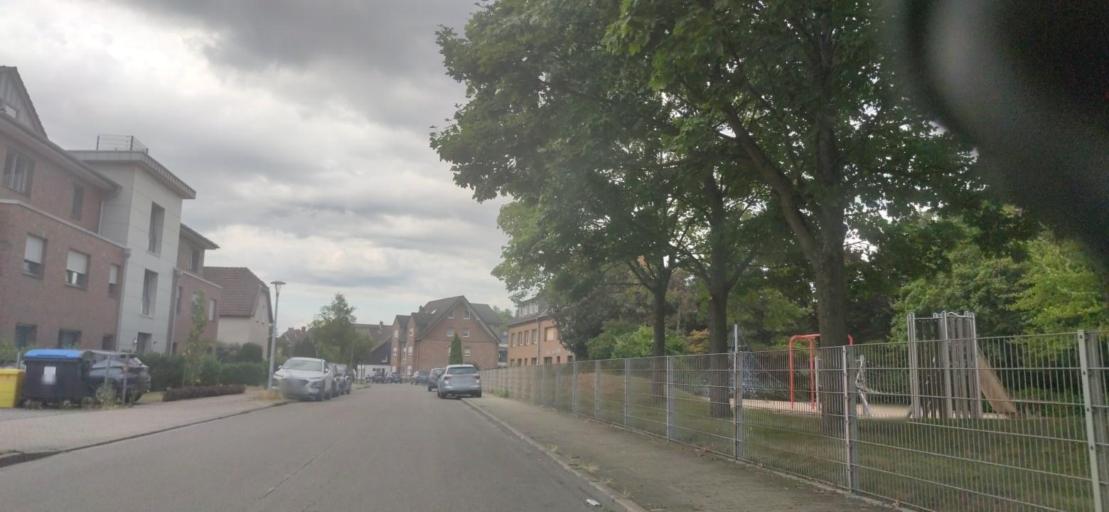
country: DE
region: North Rhine-Westphalia
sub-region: Regierungsbezirk Munster
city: Bottrop
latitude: 51.5330
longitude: 6.9532
